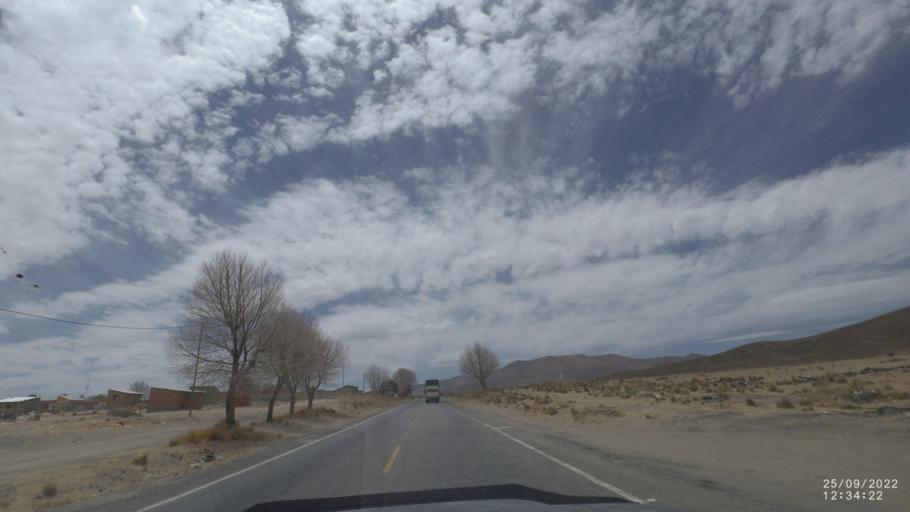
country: BO
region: Oruro
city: Machacamarca
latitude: -18.1763
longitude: -67.0151
